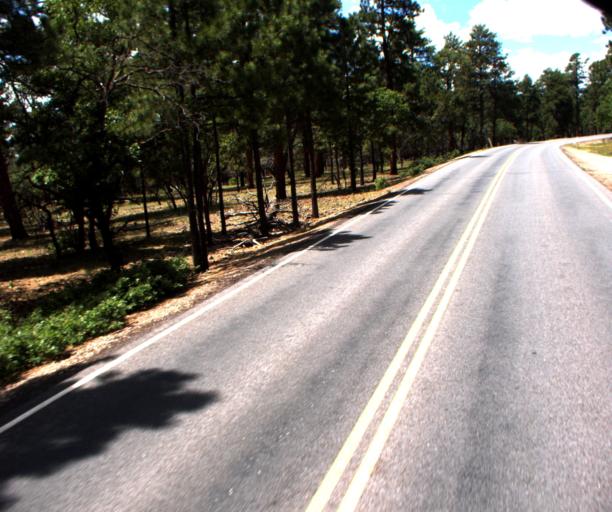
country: US
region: Arizona
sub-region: Coconino County
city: Grand Canyon
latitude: 35.9766
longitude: -111.9854
